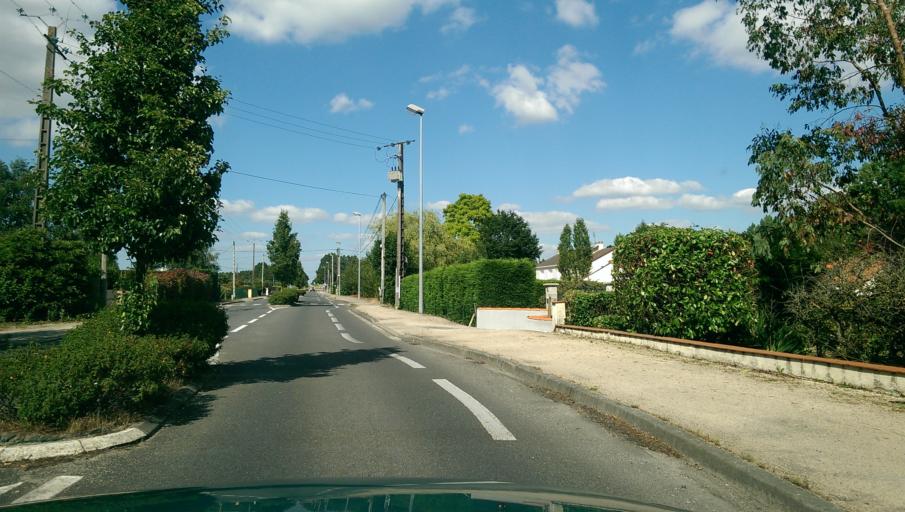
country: FR
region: Pays de la Loire
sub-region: Departement de la Loire-Atlantique
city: Lege
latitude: 46.8903
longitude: -1.5883
